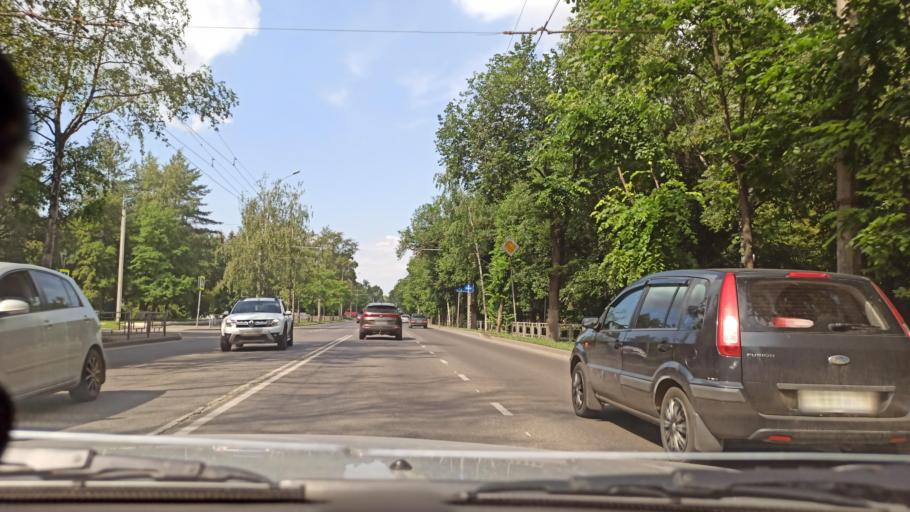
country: RU
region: Vologda
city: Vologda
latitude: 59.2198
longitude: 39.8757
